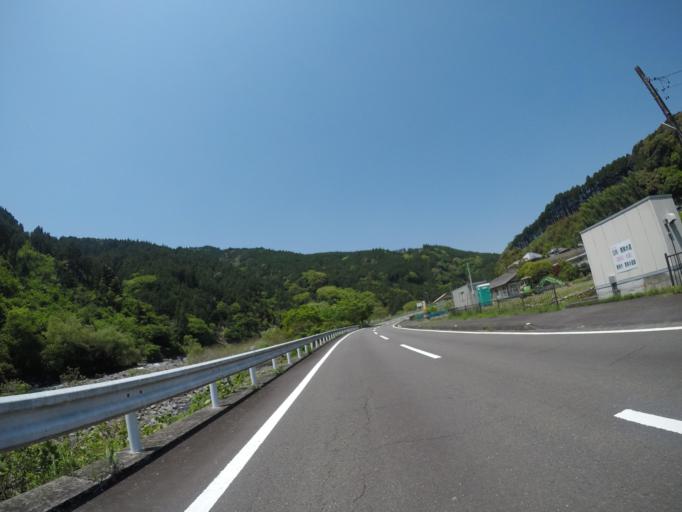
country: JP
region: Shizuoka
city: Shizuoka-shi
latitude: 35.0907
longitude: 138.2395
